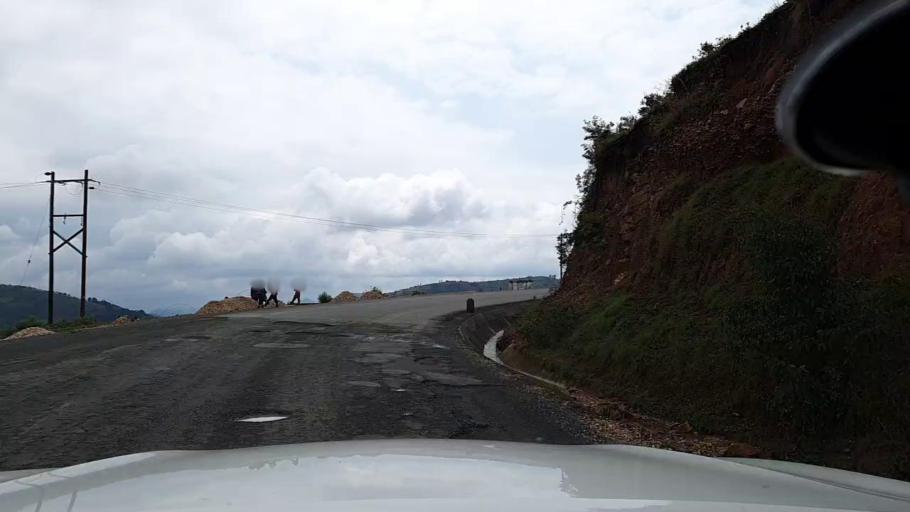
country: RW
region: Southern Province
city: Gitarama
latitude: -2.0692
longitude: 29.5603
